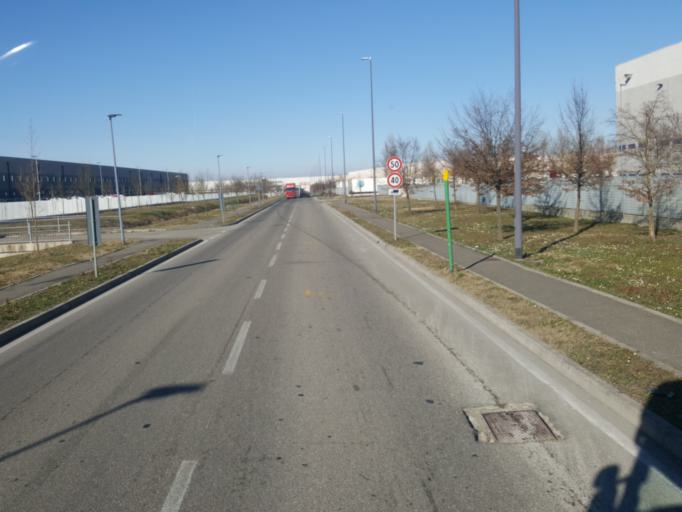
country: IT
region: Emilia-Romagna
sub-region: Provincia di Piacenza
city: Piacenza
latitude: 45.0271
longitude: 9.7509
